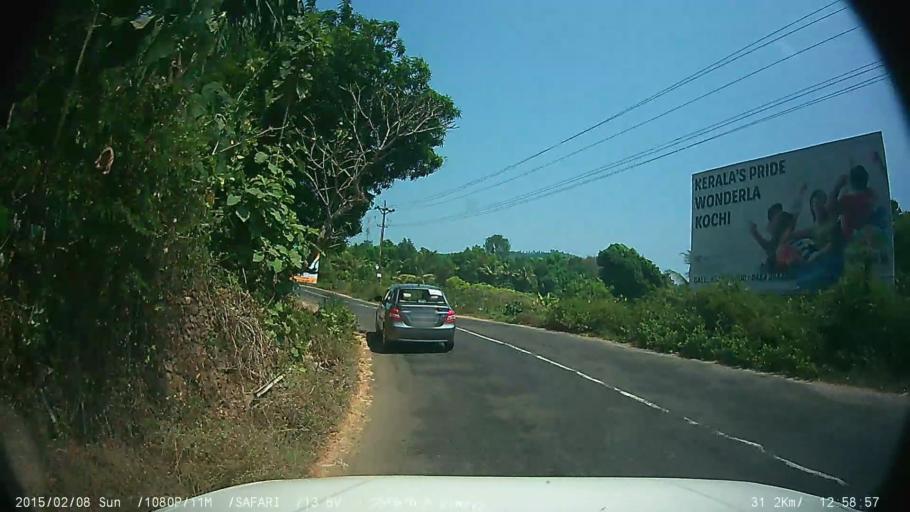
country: IN
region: Kerala
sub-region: Ernakulam
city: Muvattupuzha
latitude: 9.8982
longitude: 76.5869
